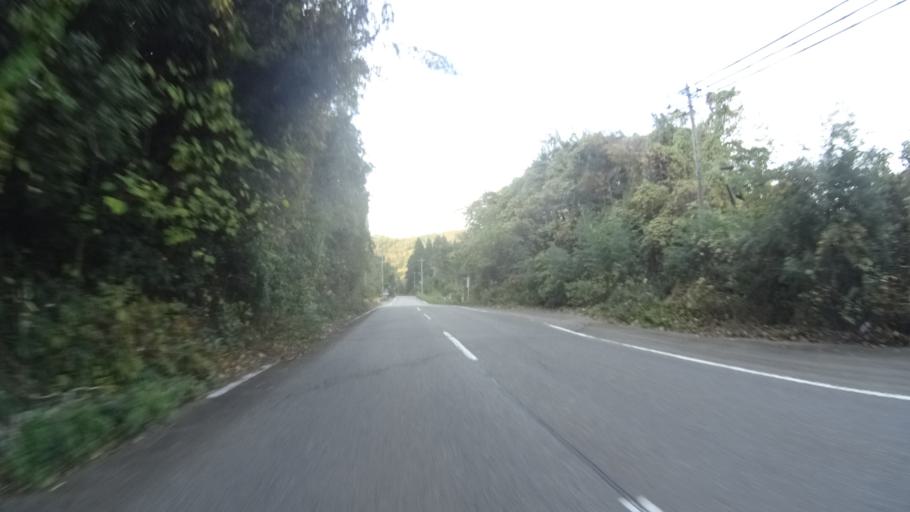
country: JP
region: Ishikawa
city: Nanao
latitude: 37.2116
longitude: 136.7067
